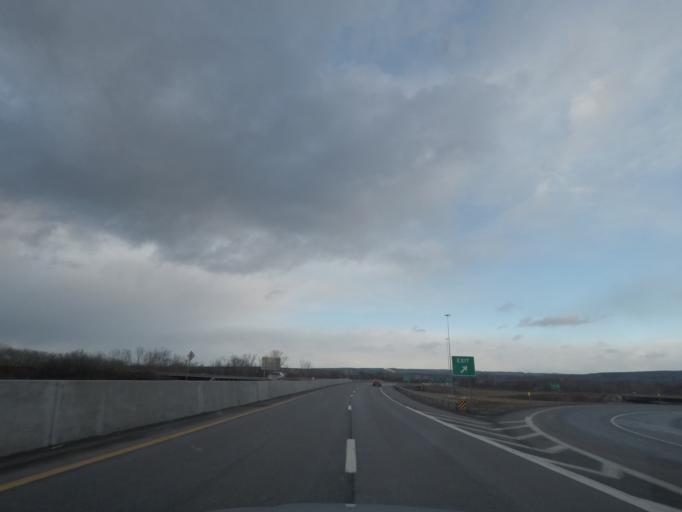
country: US
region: New York
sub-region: Oneida County
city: Utica
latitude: 43.1068
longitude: -75.2389
